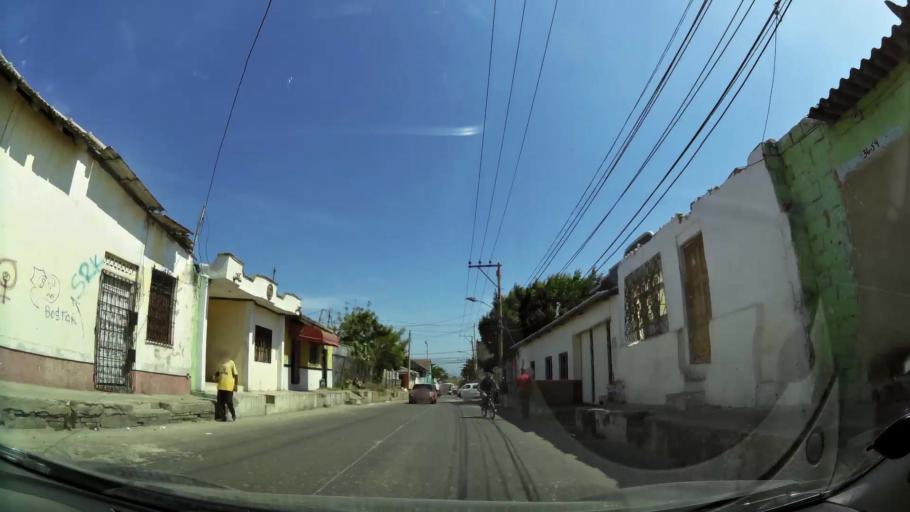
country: CO
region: Atlantico
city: Barranquilla
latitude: 10.9729
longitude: -74.7826
